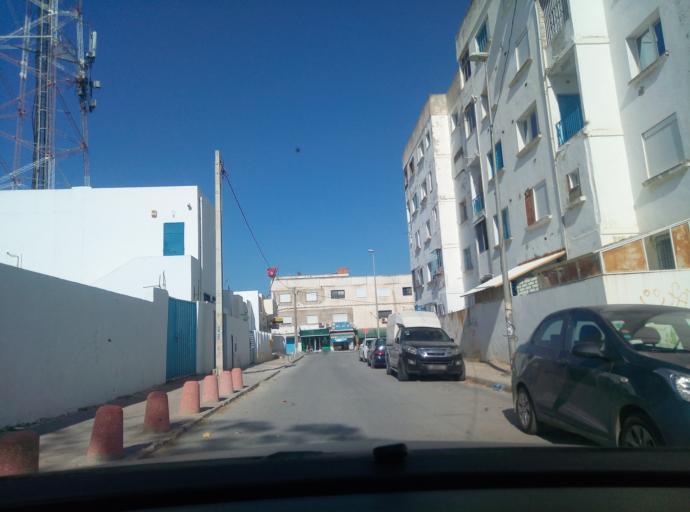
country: TN
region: Tunis
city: La Goulette
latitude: 36.8509
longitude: 10.2617
